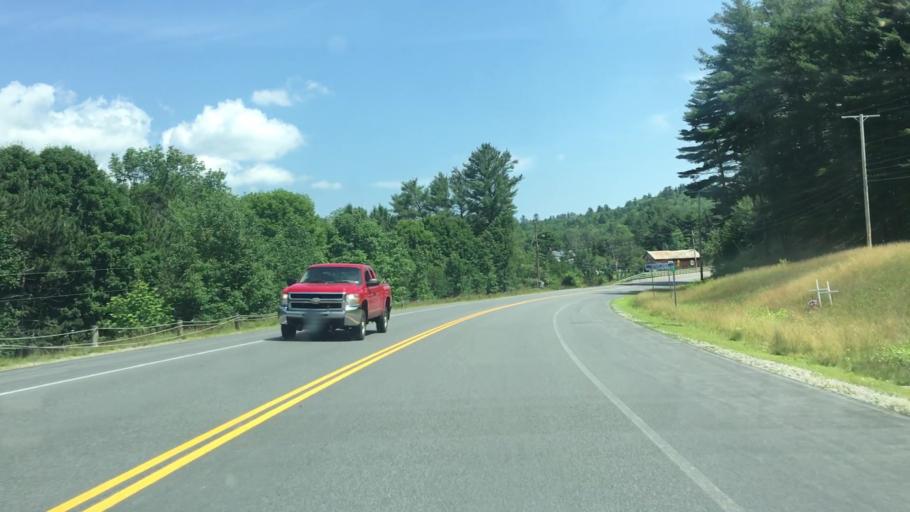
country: US
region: New Hampshire
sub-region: Sullivan County
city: Newport
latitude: 43.4133
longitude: -72.1875
